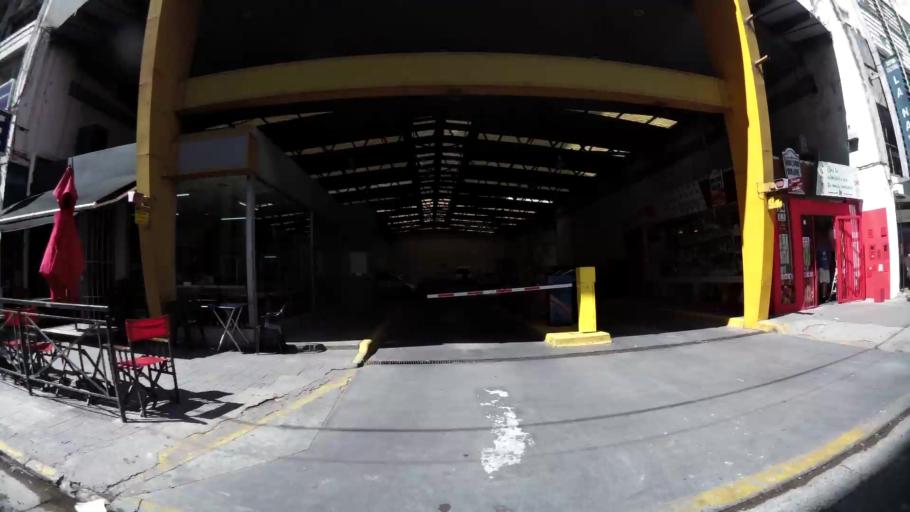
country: AR
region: Santa Fe
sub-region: Departamento de Rosario
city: Rosario
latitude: -32.9436
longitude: -60.6412
